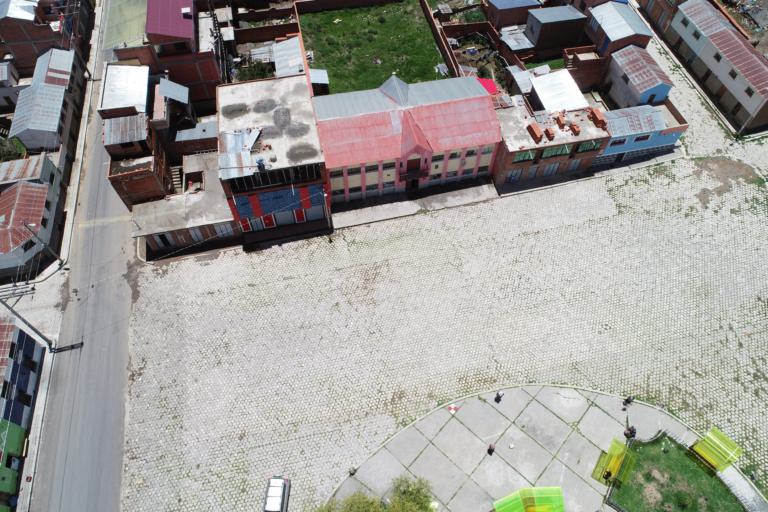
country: BO
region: La Paz
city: Achacachi
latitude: -16.0229
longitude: -68.7902
